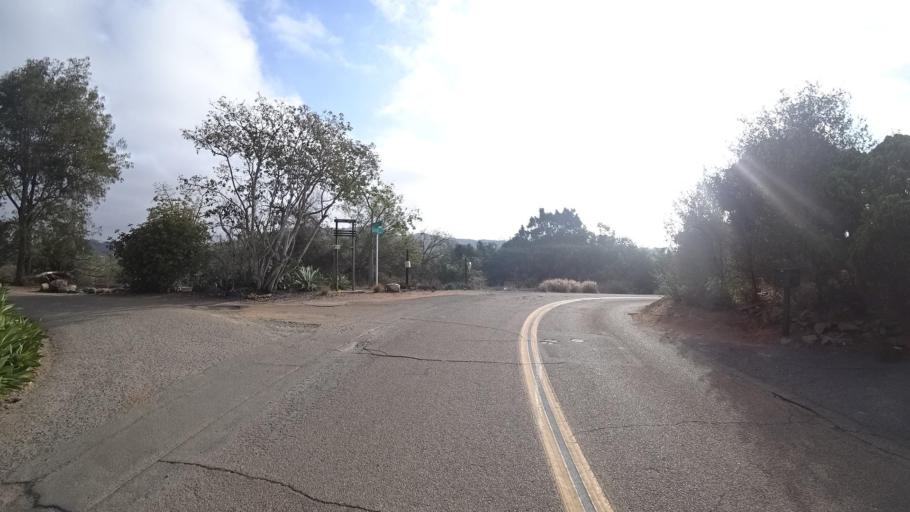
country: US
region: California
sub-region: San Diego County
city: Vista
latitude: 33.2007
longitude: -117.2090
